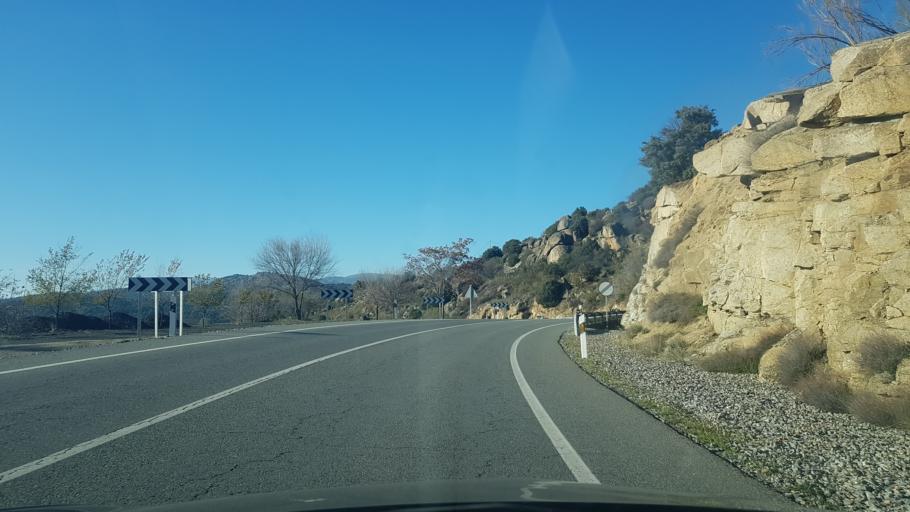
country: ES
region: Castille and Leon
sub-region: Provincia de Avila
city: El Tiemblo
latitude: 40.4363
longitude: -4.5554
